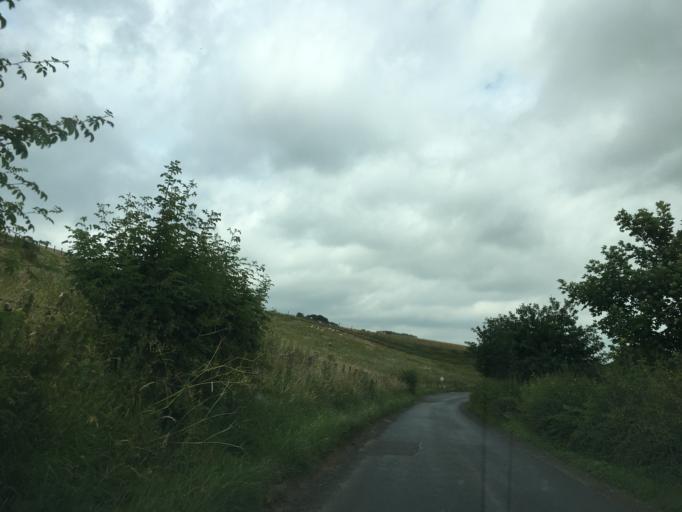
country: GB
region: Scotland
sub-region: The Scottish Borders
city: Peebles
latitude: 55.6689
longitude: -3.2046
